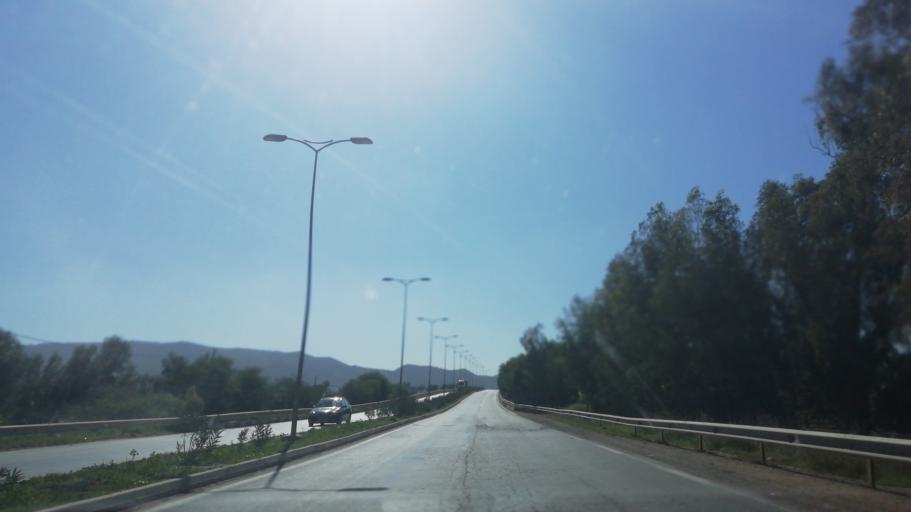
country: DZ
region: Mascara
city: Sig
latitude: 35.5421
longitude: -0.2045
